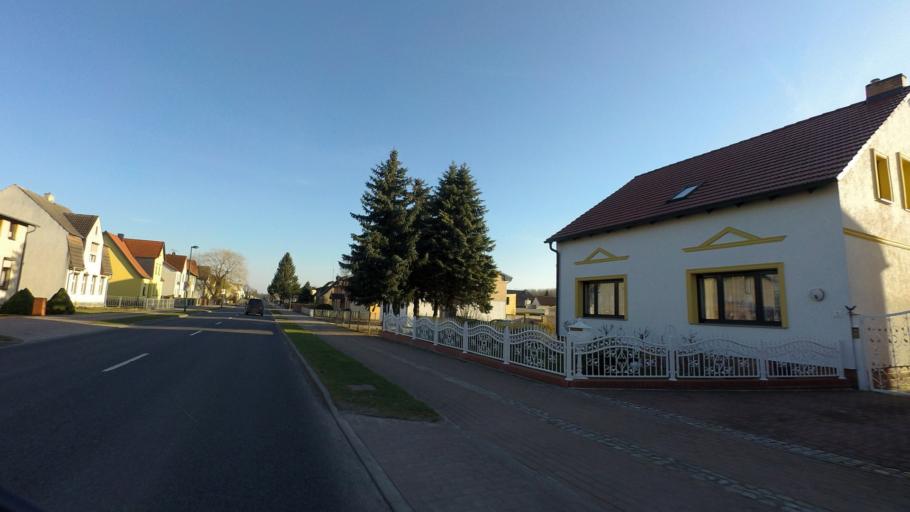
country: DE
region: Brandenburg
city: Britz
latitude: 52.8786
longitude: 13.8178
